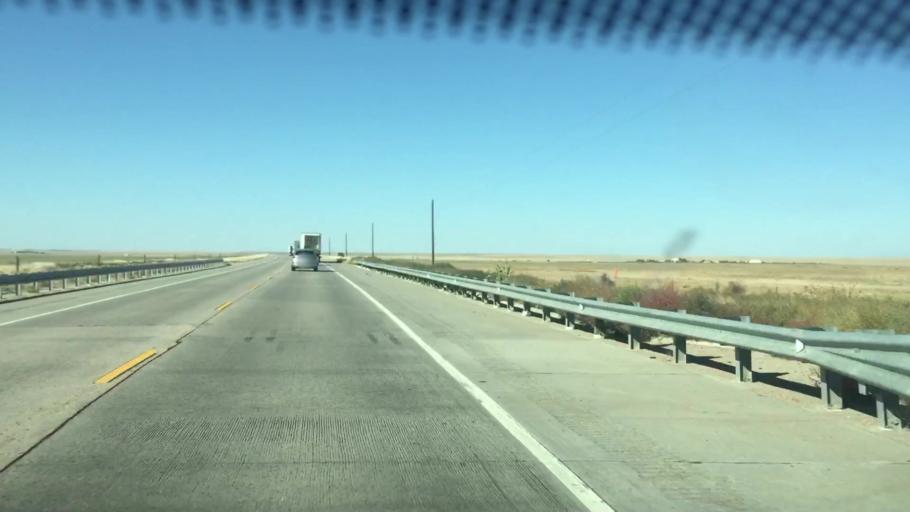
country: US
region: Colorado
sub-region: Kiowa County
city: Eads
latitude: 38.3334
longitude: -102.7199
